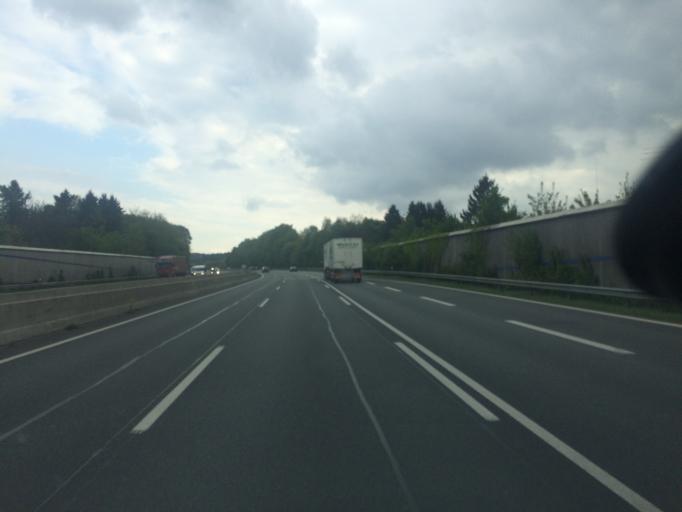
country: DE
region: North Rhine-Westphalia
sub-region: Regierungsbezirk Detmold
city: Oerlinghausen
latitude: 51.9893
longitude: 8.6157
